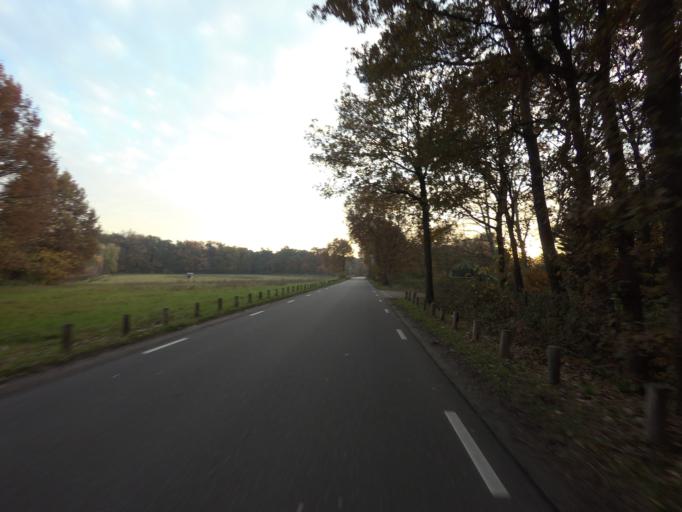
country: NL
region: North Brabant
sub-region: Gemeente Breda
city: Breda
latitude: 51.5215
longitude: 4.7623
